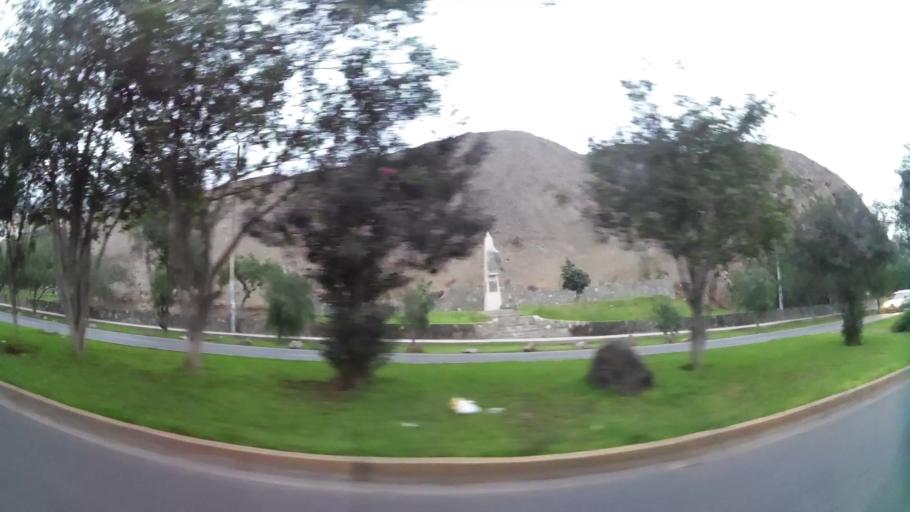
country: PE
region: Lima
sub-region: Lima
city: La Molina
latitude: -12.1089
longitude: -76.9435
